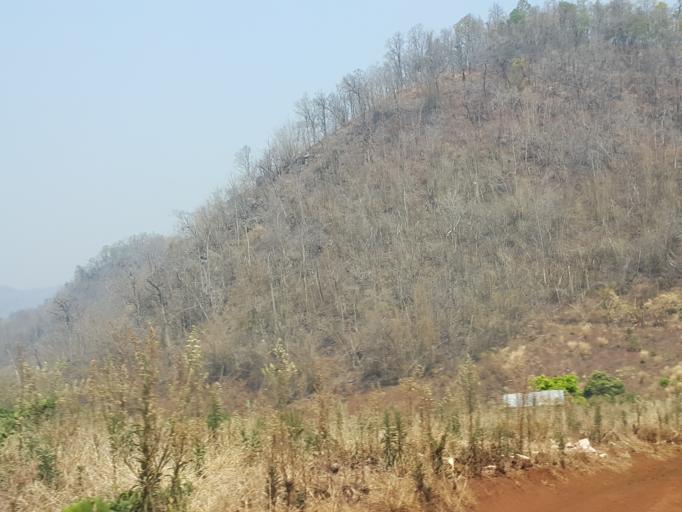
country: TH
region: Chiang Mai
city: Samoeng
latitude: 18.7736
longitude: 98.8222
